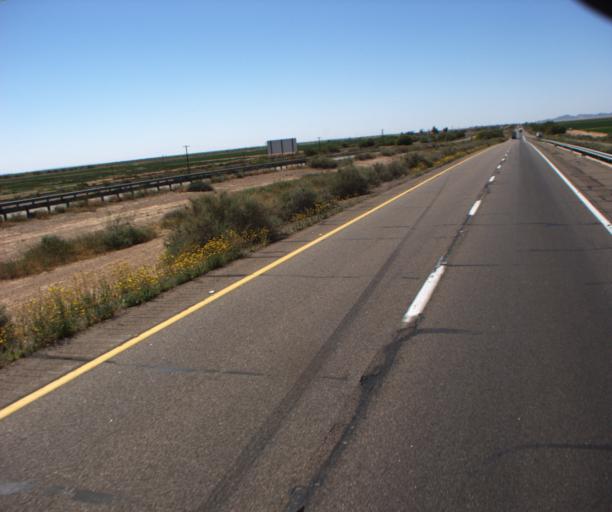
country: US
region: Arizona
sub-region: Maricopa County
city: Gila Bend
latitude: 32.9324
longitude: -112.8047
